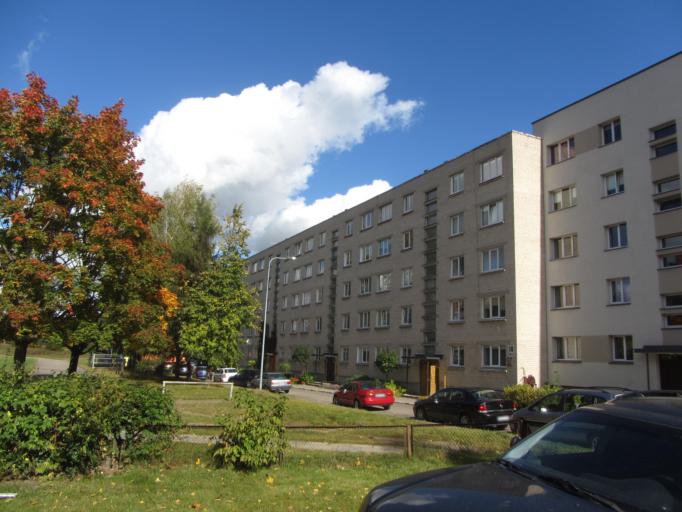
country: LT
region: Utenos apskritis
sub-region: Utena
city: Utena
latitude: 55.5041
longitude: 25.6147
